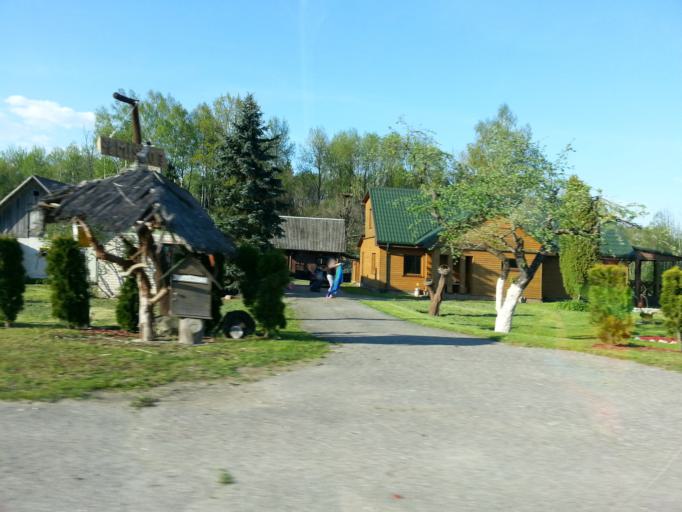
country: LT
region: Vilnius County
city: Ukmerge
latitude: 55.4027
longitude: 24.6857
